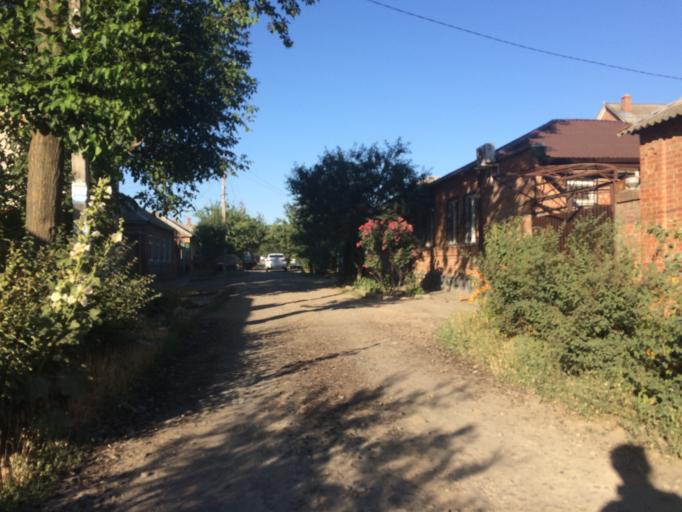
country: RU
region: Rostov
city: Rostov-na-Donu
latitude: 47.2172
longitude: 39.6375
